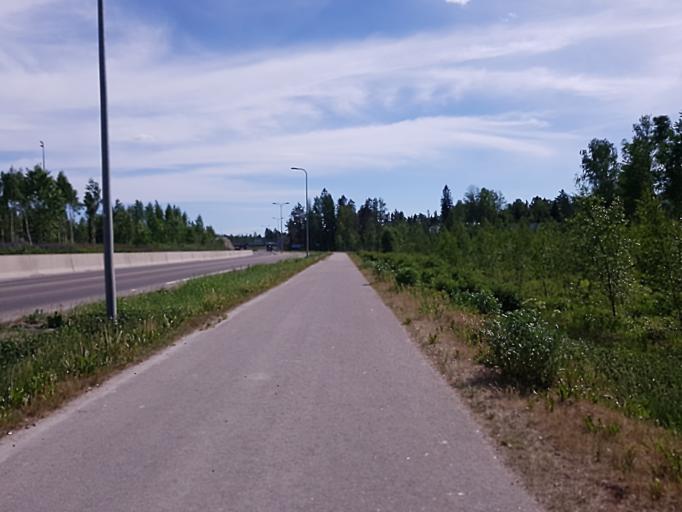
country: FI
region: Uusimaa
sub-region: Helsinki
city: Vantaa
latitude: 60.3010
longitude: 24.9160
